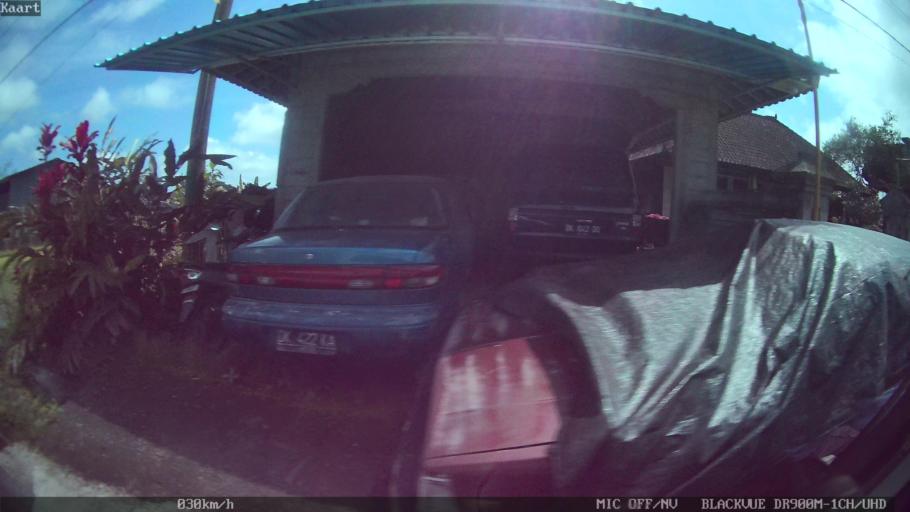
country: ID
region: Bali
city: Banjar Apuan Kaja
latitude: -8.4962
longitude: 115.3415
